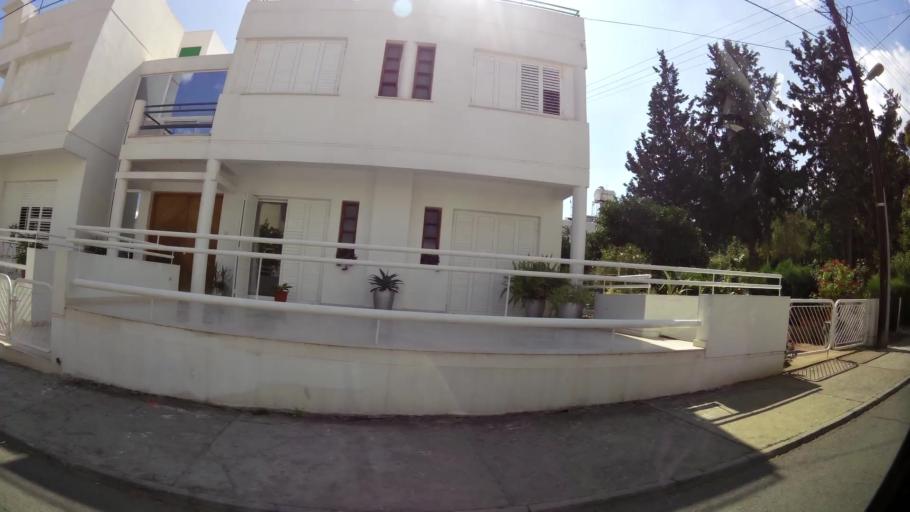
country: CY
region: Larnaka
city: Larnaca
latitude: 34.9084
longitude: 33.6263
